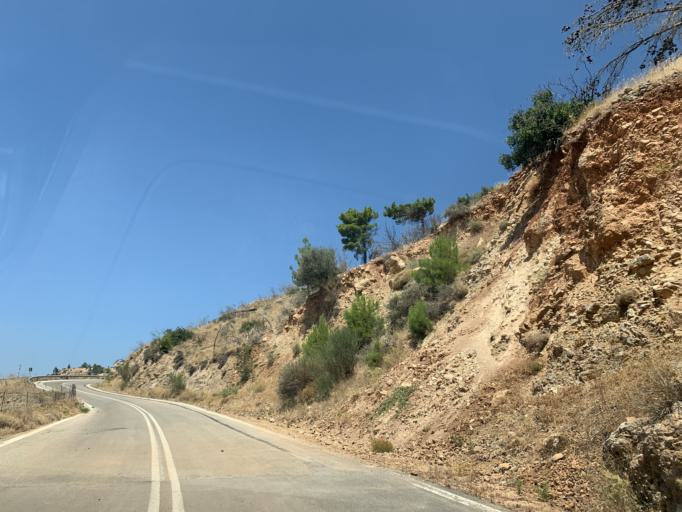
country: GR
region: North Aegean
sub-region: Chios
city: Vrontados
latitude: 38.4508
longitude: 25.9786
